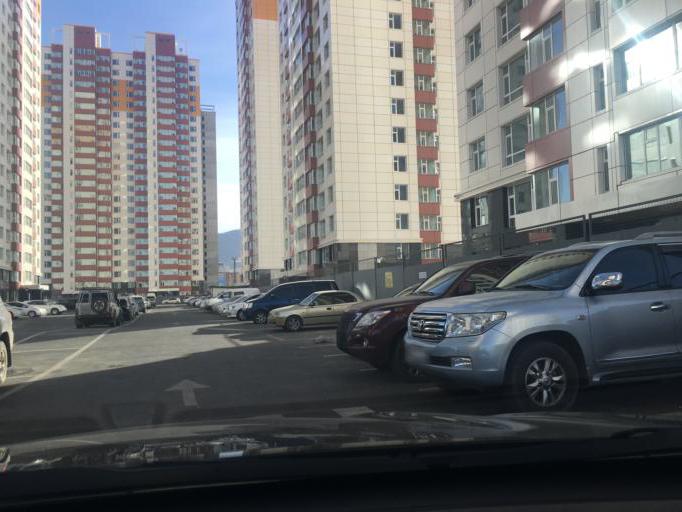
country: MN
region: Ulaanbaatar
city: Ulaanbaatar
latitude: 47.9061
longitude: 106.8963
